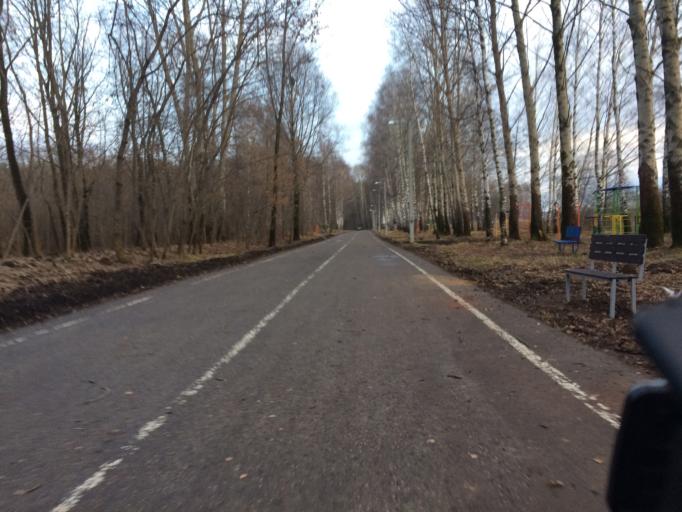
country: RU
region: Mariy-El
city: Yoshkar-Ola
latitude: 56.6235
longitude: 47.9140
